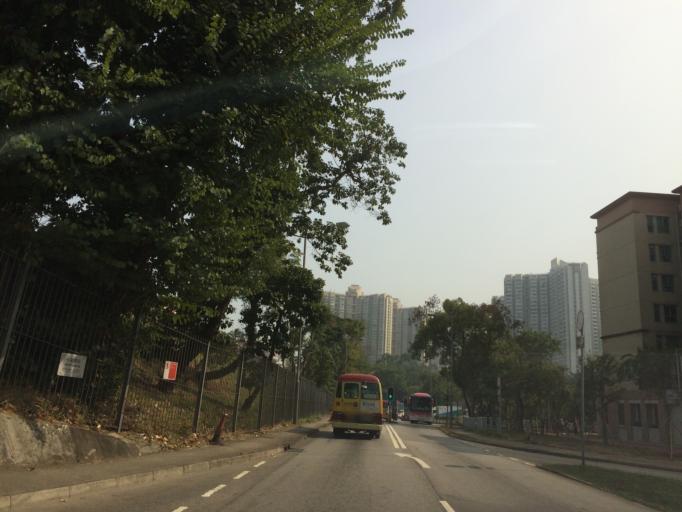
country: HK
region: Tai Po
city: Tai Po
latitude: 22.4541
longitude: 114.1557
